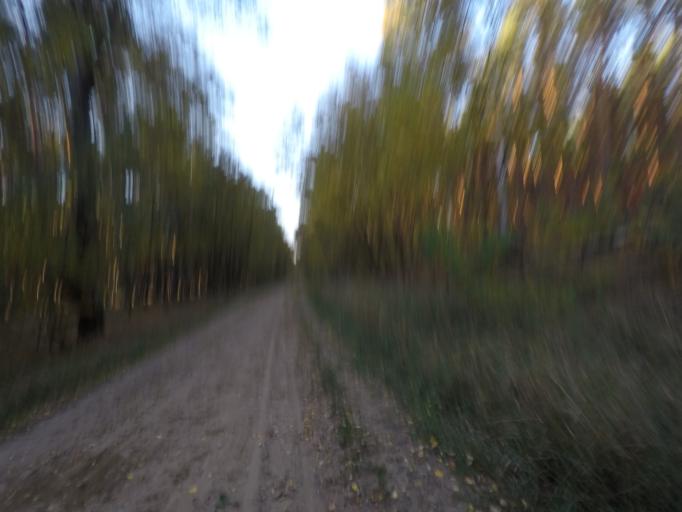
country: DE
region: Brandenburg
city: Biesenthal
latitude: 52.7833
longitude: 13.6386
